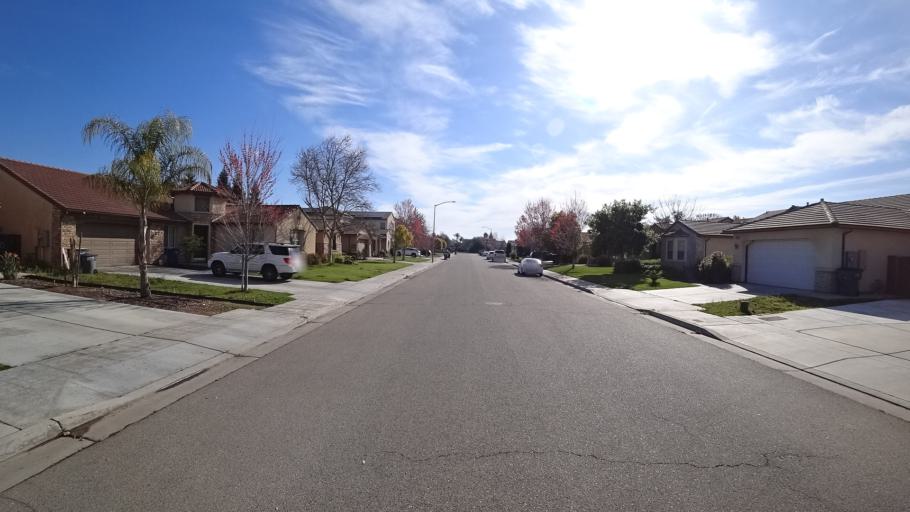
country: US
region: California
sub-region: Fresno County
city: West Park
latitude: 36.7987
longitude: -119.8961
